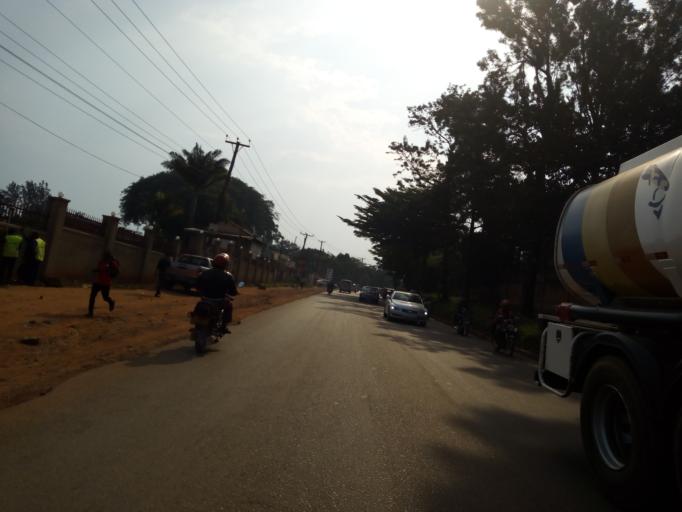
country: UG
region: Central Region
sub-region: Wakiso District
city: Kireka
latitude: 0.3186
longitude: 32.6273
